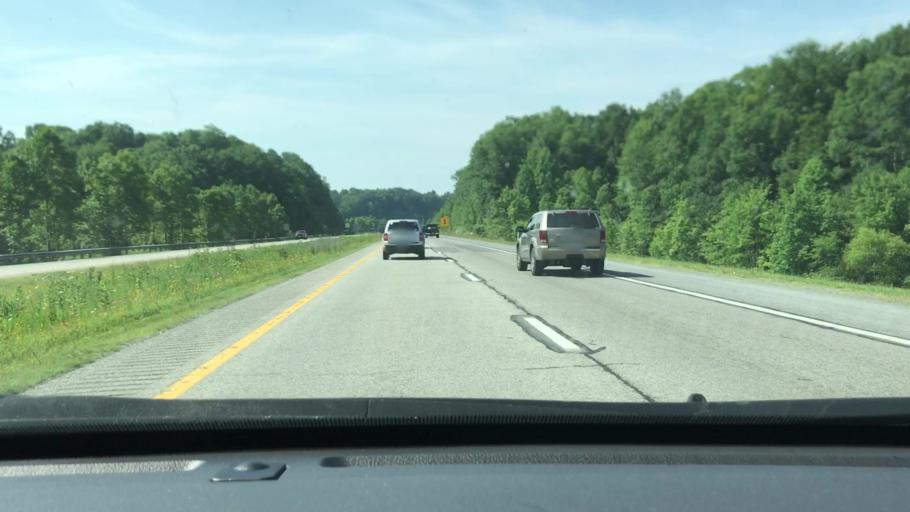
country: US
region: West Virginia
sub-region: Fayette County
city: Fayetteville
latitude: 38.0222
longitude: -81.1233
